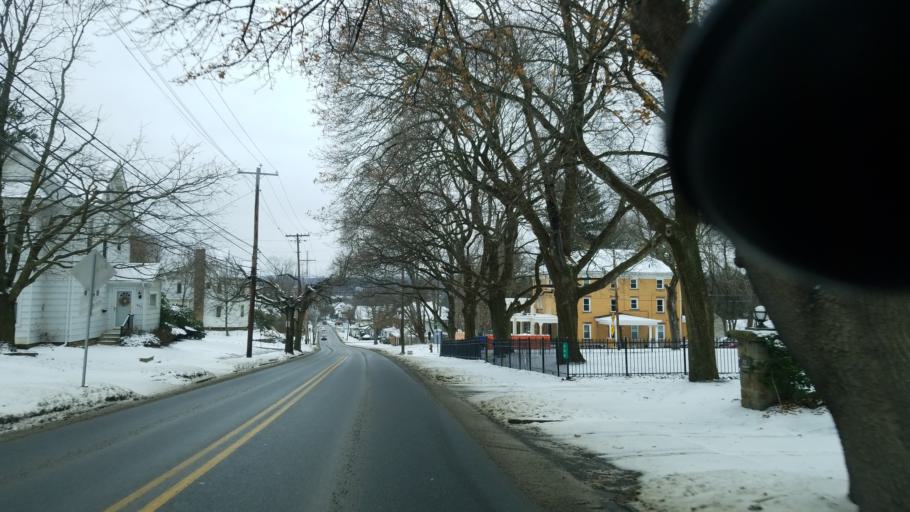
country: US
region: Pennsylvania
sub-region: Jefferson County
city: Punxsutawney
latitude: 40.9440
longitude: -78.9581
